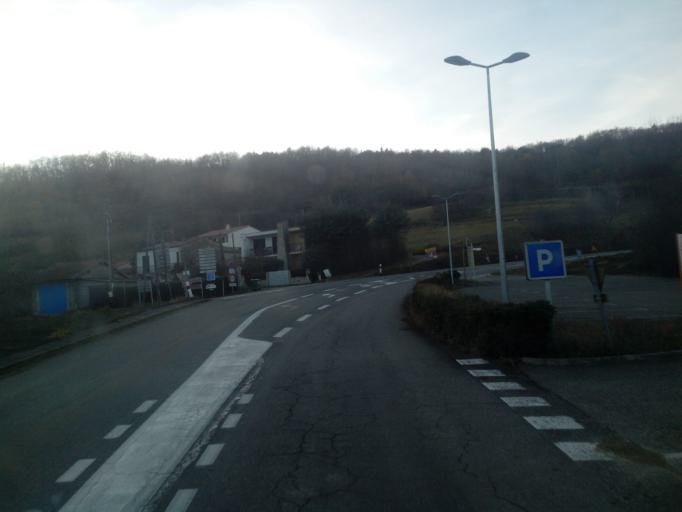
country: FR
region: Languedoc-Roussillon
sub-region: Departement de l'Aude
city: Chalabre
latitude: 42.9207
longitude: 2.0454
